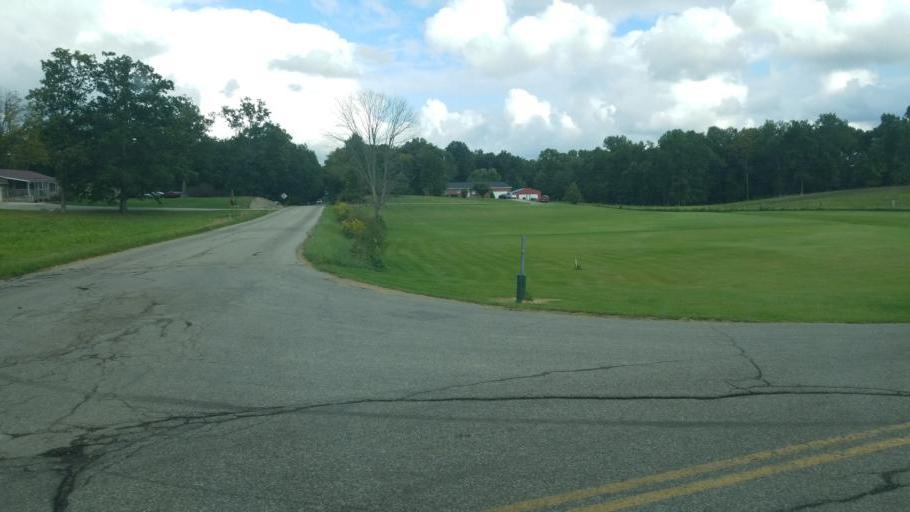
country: US
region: Ohio
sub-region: Jackson County
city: Oak Hill
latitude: 38.9426
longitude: -82.6030
